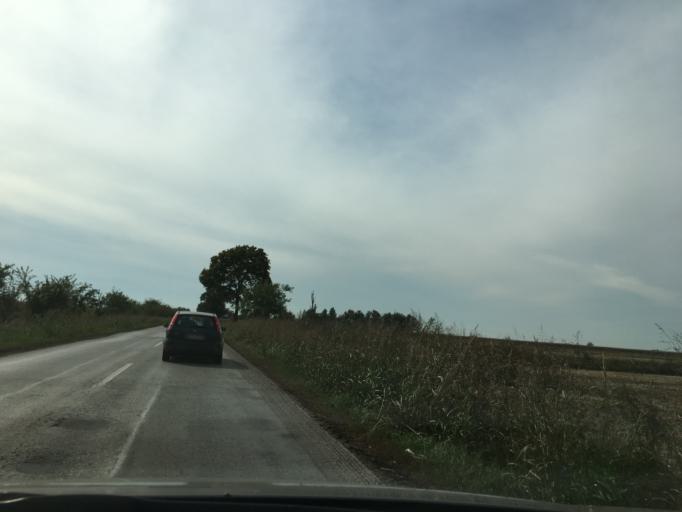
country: RS
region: Autonomna Pokrajina Vojvodina
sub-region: Juznobacki Okrug
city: Temerin
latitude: 45.4518
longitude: 19.9071
